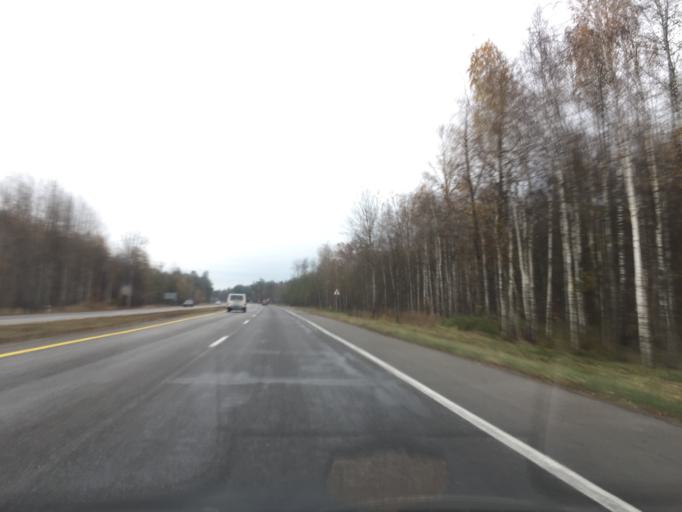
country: BY
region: Gomel
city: Kastsyukowka
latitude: 52.3569
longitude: 30.6984
